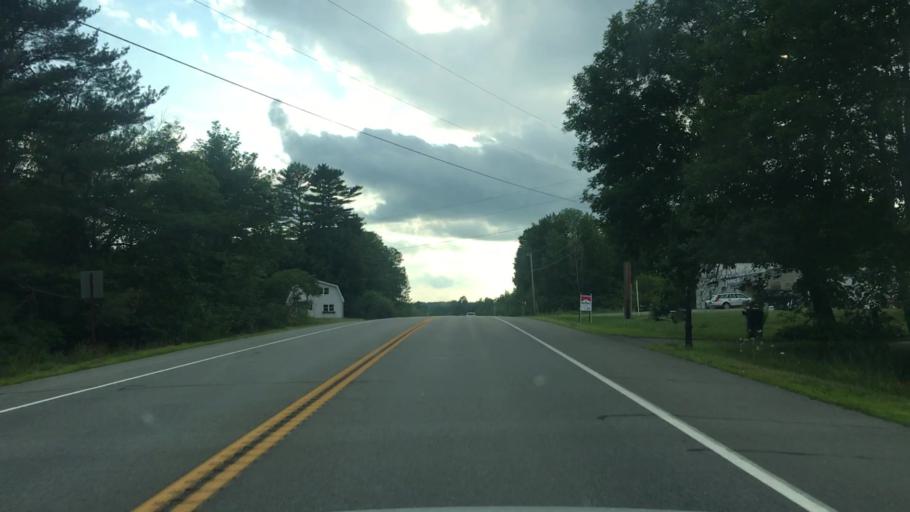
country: US
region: Maine
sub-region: Kennebec County
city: Windsor
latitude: 44.3859
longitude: -69.6011
